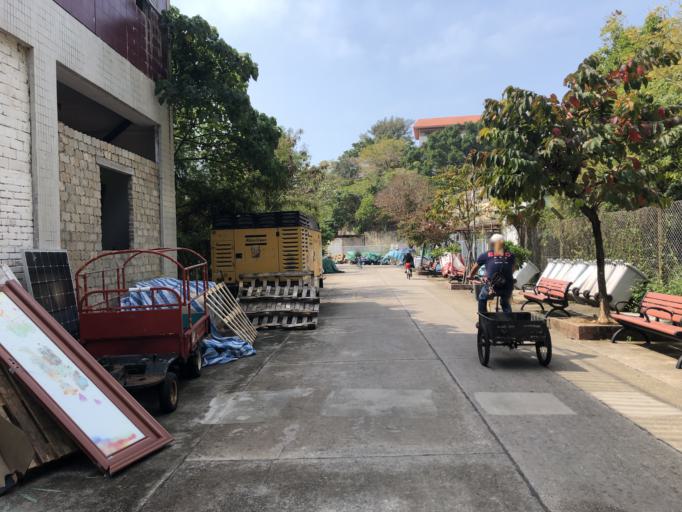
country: HK
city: Yung Shue Wan
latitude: 22.2123
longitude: 114.0257
